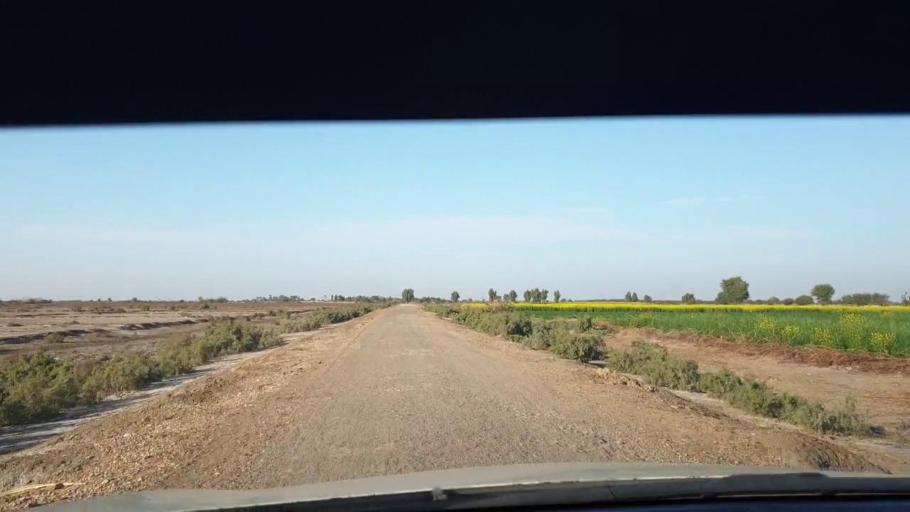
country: PK
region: Sindh
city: Berani
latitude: 25.8150
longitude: 68.9100
